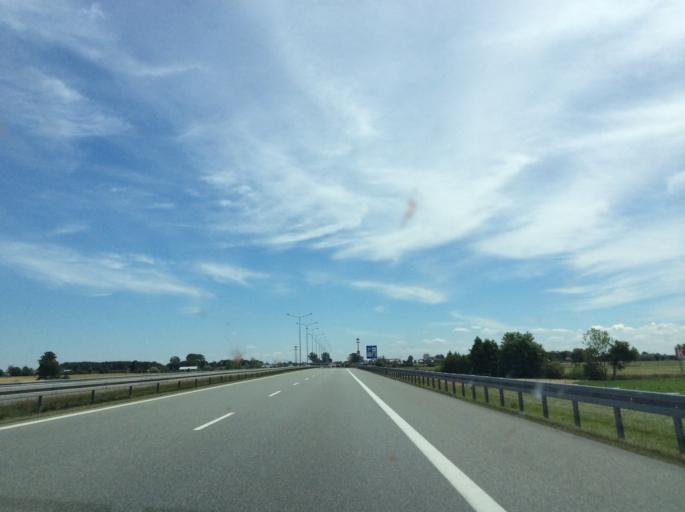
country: PL
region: Greater Poland Voivodeship
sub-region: Powiat poznanski
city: Buk
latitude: 52.3885
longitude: 16.4661
